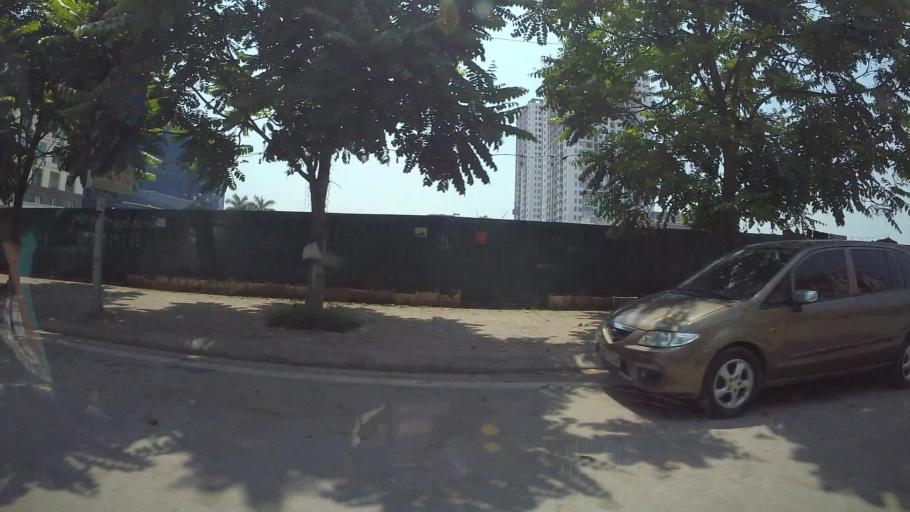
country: VN
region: Ha Noi
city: Hoan Kiem
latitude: 21.0405
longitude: 105.8759
